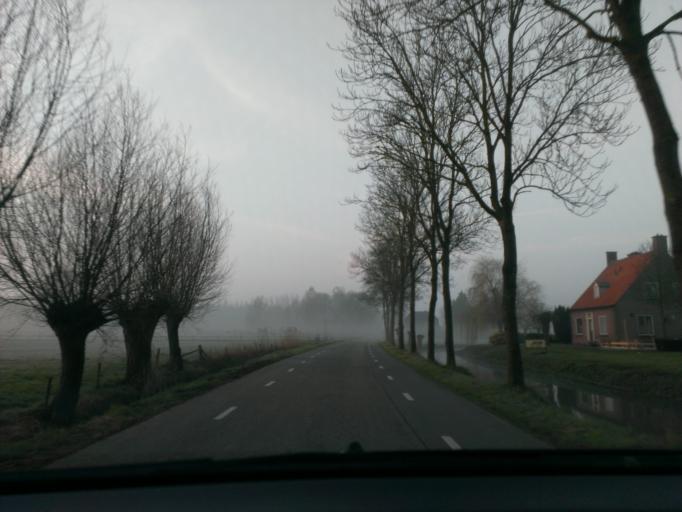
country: NL
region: Gelderland
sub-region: Gemeente Voorst
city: Twello
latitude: 52.2587
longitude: 6.0850
